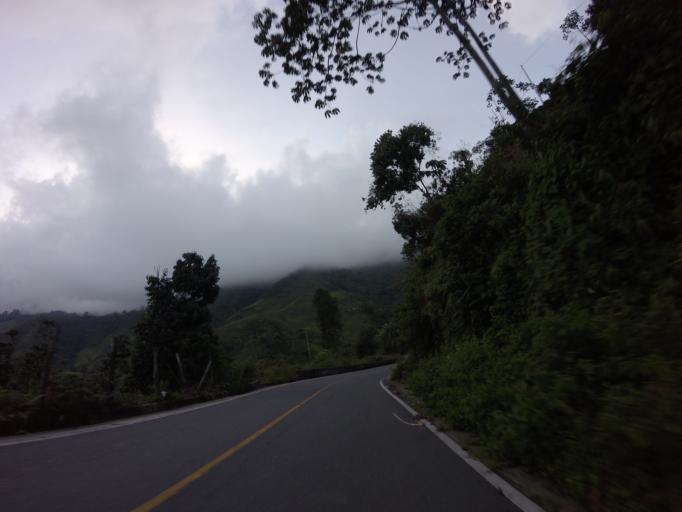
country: CO
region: Caldas
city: Manzanares
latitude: 5.3125
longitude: -75.1342
